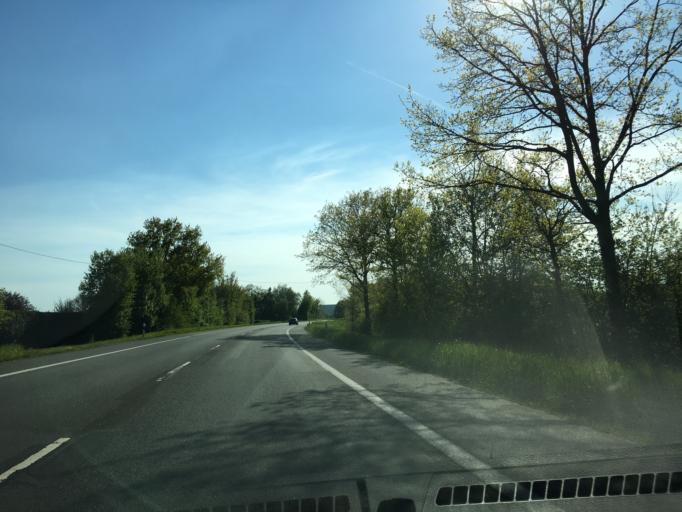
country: DE
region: North Rhine-Westphalia
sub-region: Regierungsbezirk Munster
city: Senden
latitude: 51.9146
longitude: 7.4956
